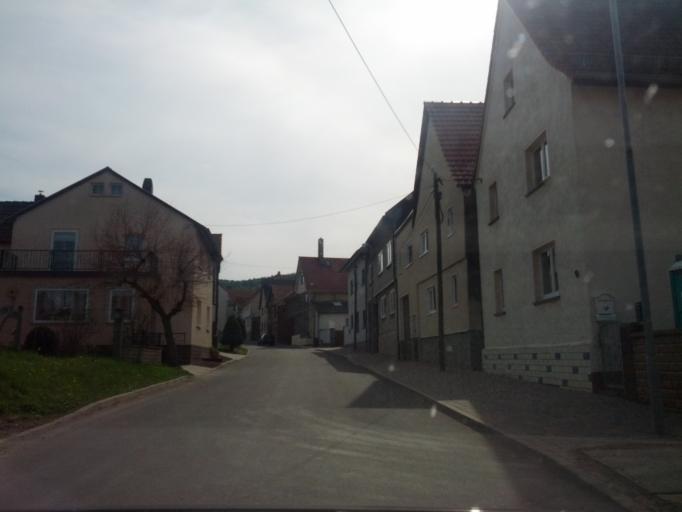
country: DE
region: Thuringia
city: Haina
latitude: 50.9632
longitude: 10.4800
